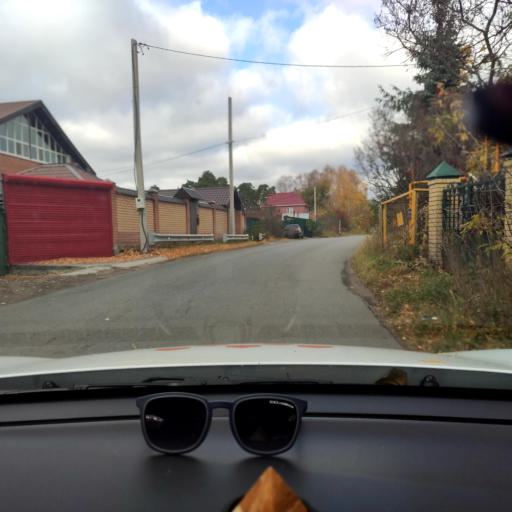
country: RU
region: Tatarstan
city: Verkhniy Uslon
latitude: 55.6186
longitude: 49.0147
